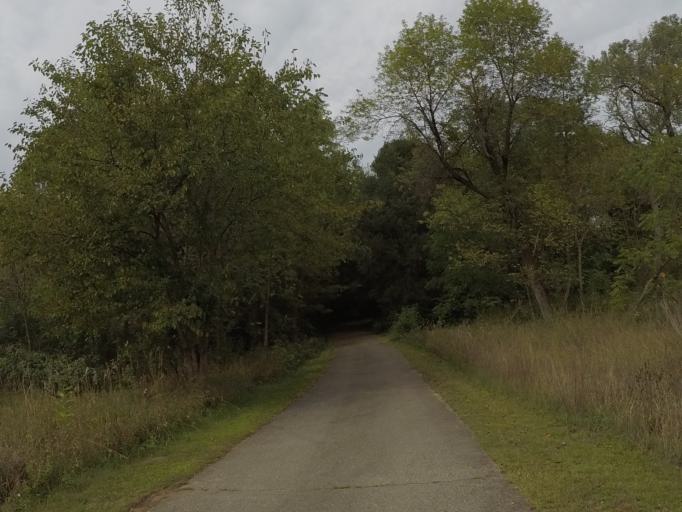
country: US
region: Wisconsin
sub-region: Sauk County
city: Sauk City
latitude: 43.2765
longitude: -89.7190
